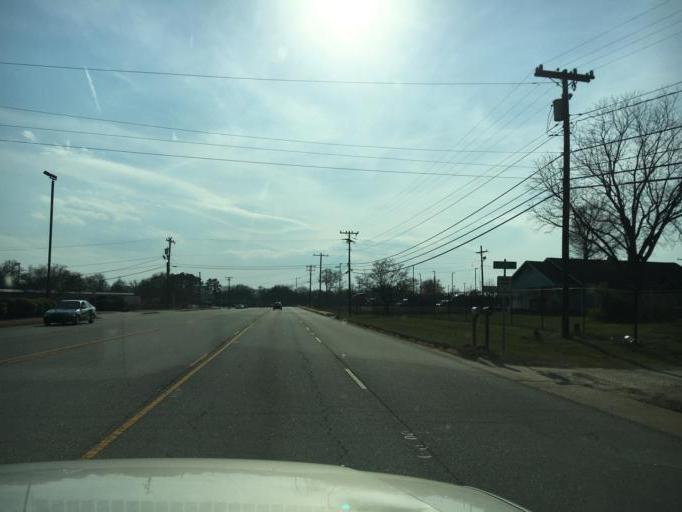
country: US
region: South Carolina
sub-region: Spartanburg County
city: Spartanburg
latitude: 35.0132
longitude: -81.9013
